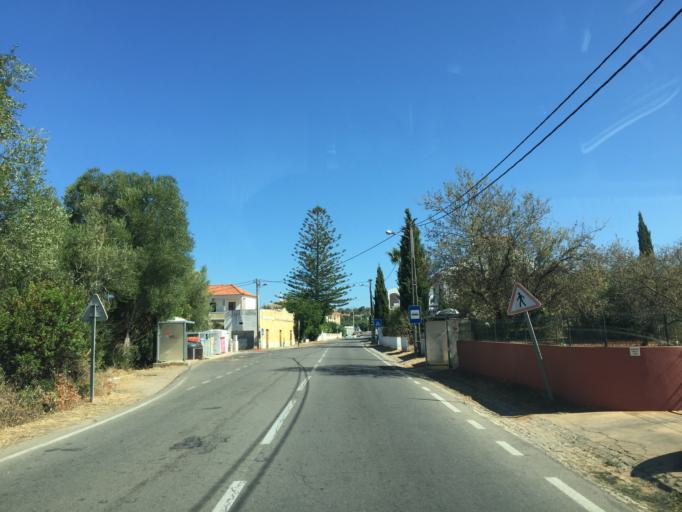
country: PT
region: Faro
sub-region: Loule
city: Almancil
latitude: 37.1008
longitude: -8.0421
